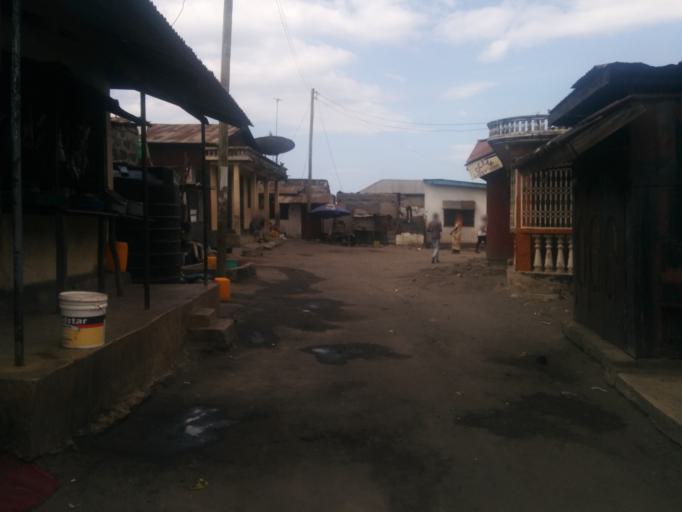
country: TZ
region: Dar es Salaam
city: Magomeni
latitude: -6.7988
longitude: 39.2366
